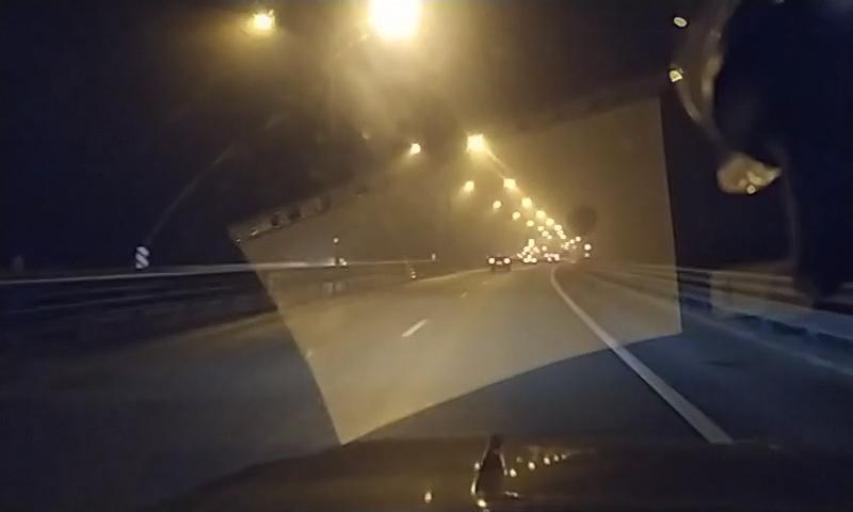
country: RU
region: Leningrad
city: Bugry
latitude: 60.1136
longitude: 30.3866
